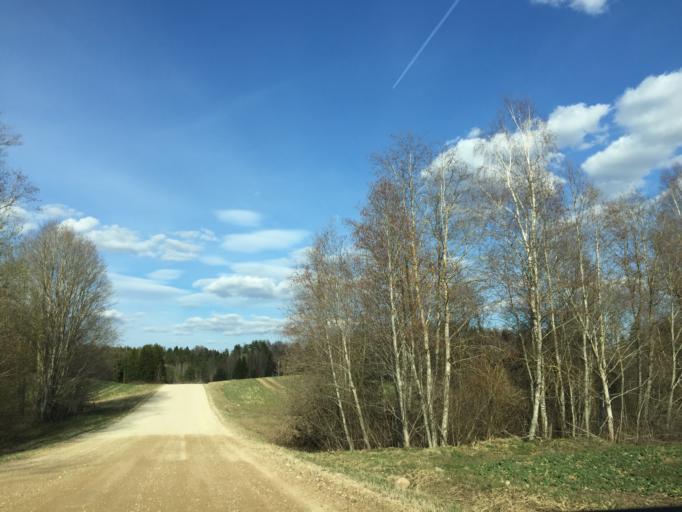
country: EE
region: Tartu
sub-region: Noo vald
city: Noo
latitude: 58.1160
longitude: 26.5593
